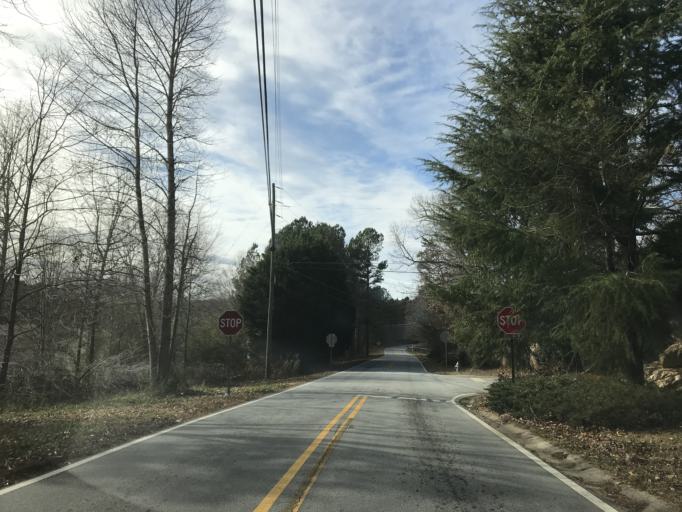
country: US
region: Georgia
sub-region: Douglas County
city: Douglasville
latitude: 33.7962
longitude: -84.8208
